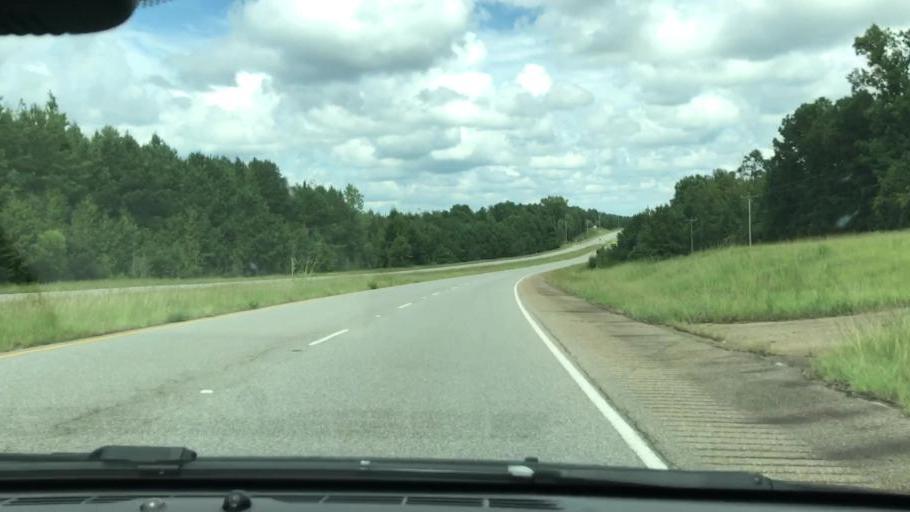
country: US
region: Georgia
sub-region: Stewart County
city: Lumpkin
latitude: 32.1252
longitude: -84.8222
